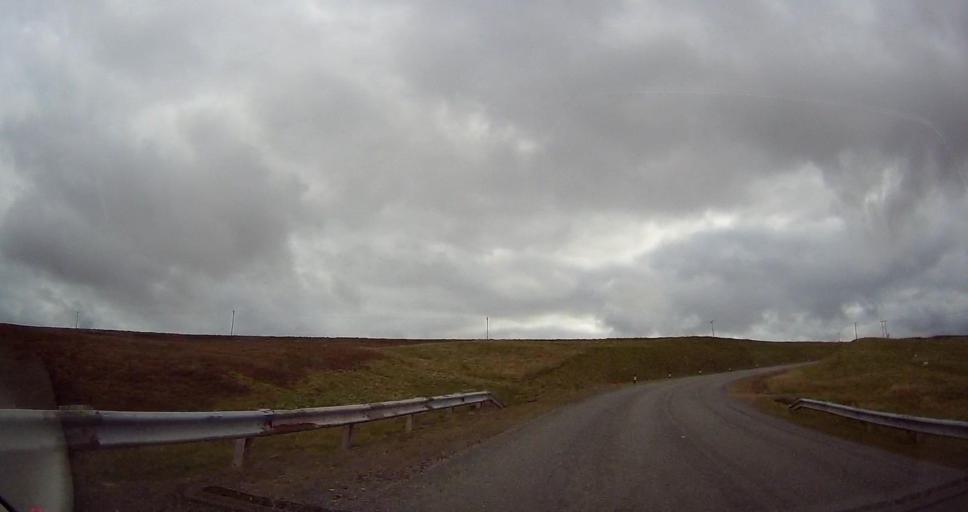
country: GB
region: Scotland
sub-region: Shetland Islands
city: Shetland
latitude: 60.6695
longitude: -1.0664
